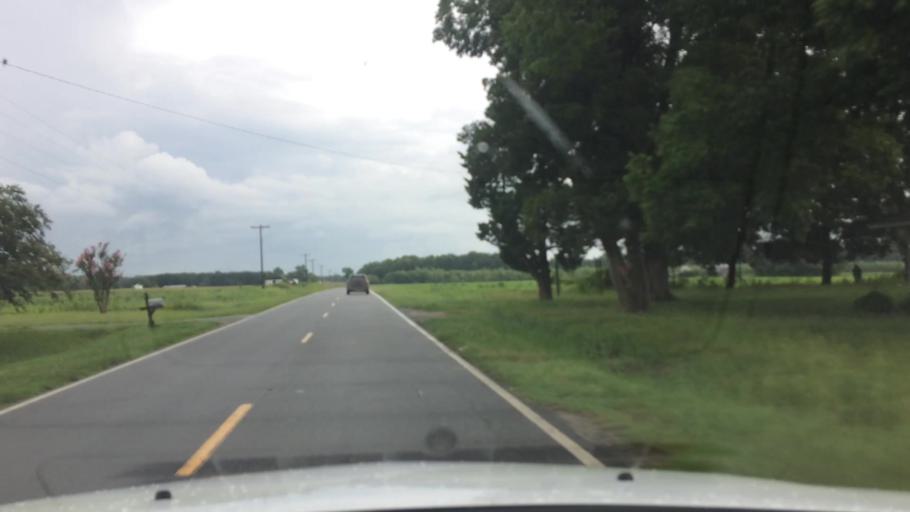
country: US
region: North Carolina
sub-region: Pitt County
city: Farmville
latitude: 35.5629
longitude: -77.5471
